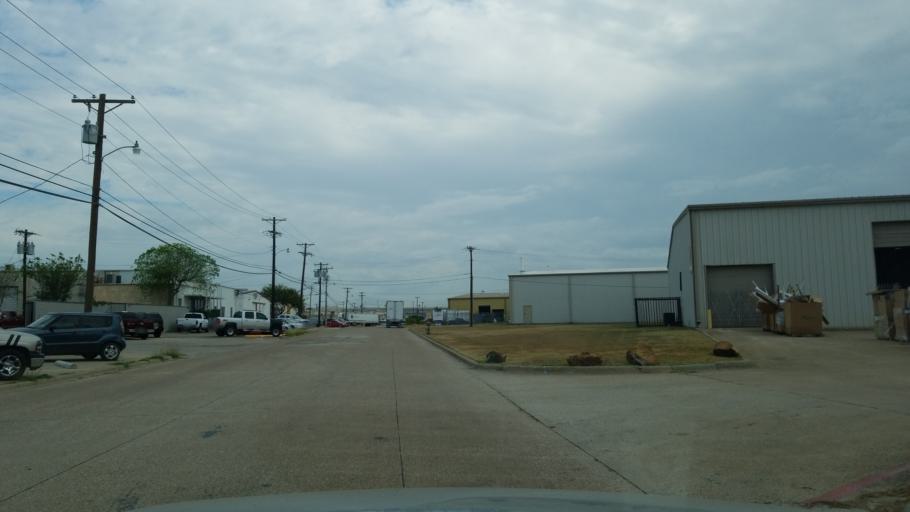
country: US
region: Texas
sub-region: Dallas County
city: Garland
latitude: 32.9040
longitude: -96.6874
